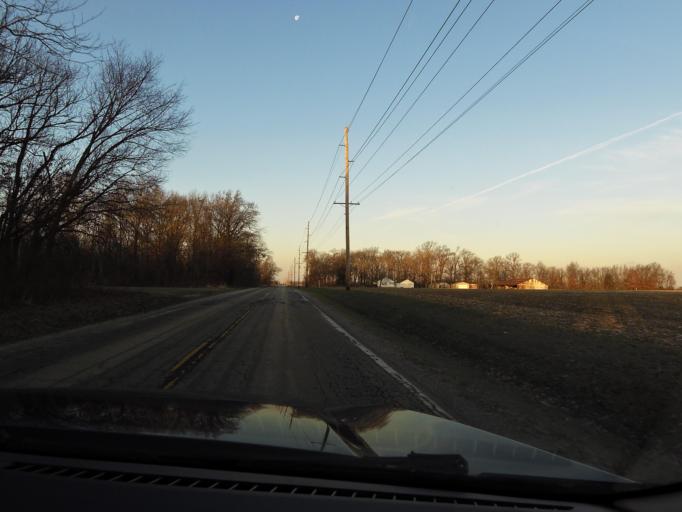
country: US
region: Illinois
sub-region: Marion County
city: Odin
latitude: 38.7650
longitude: -89.0602
